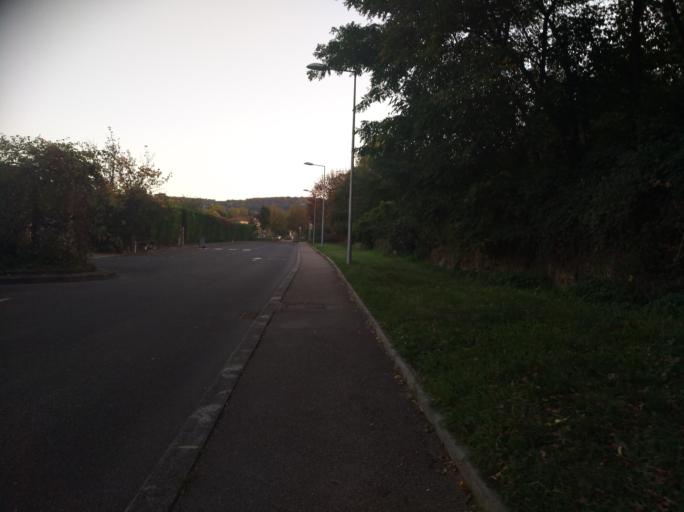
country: FR
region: Rhone-Alpes
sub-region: Departement du Rhone
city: Chasselay
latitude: 45.8873
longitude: 4.8033
